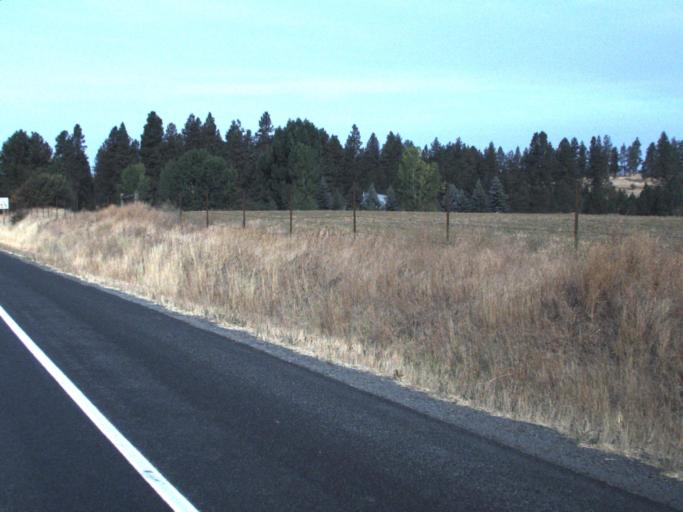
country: US
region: Idaho
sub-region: Benewah County
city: Plummer
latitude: 47.4350
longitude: -117.0412
